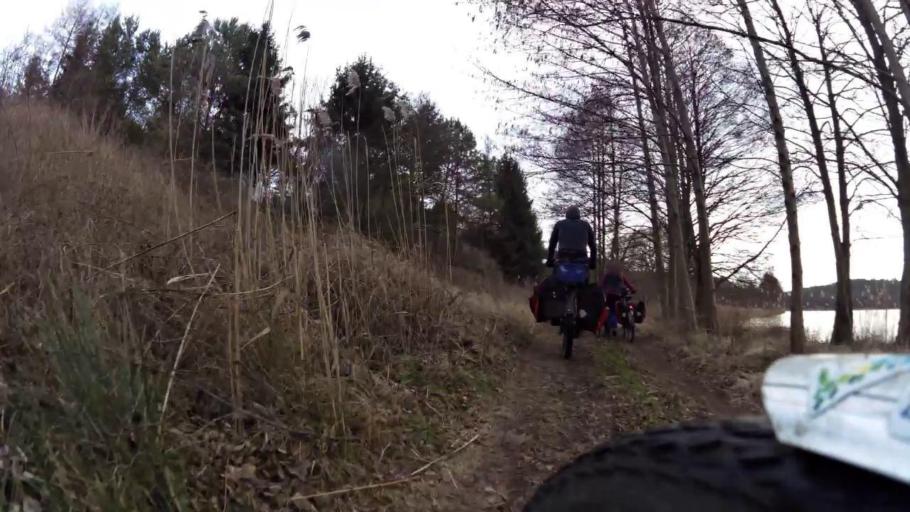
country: PL
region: West Pomeranian Voivodeship
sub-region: Powiat kamienski
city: Wolin
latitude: 53.9612
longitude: 14.5760
